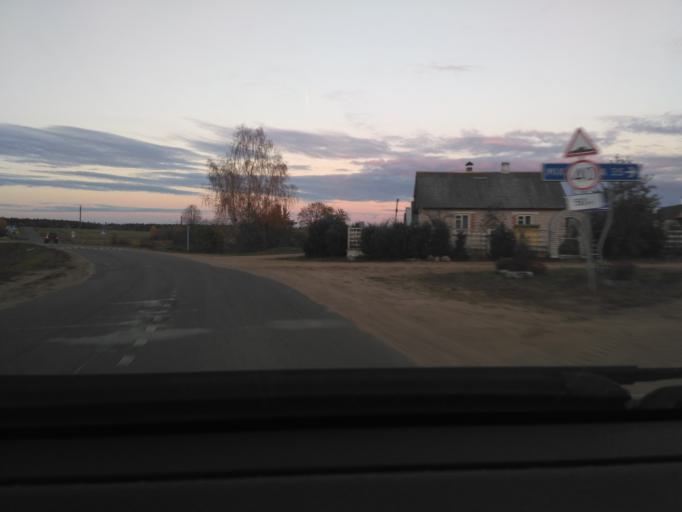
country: BY
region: Minsk
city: Loshnitsa
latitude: 54.3601
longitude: 28.6237
